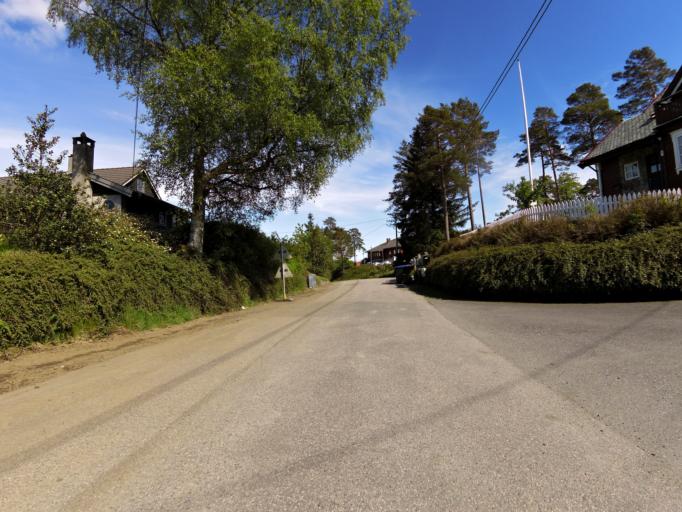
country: NO
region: Hordaland
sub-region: Stord
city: Leirvik
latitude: 59.7875
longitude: 5.4923
